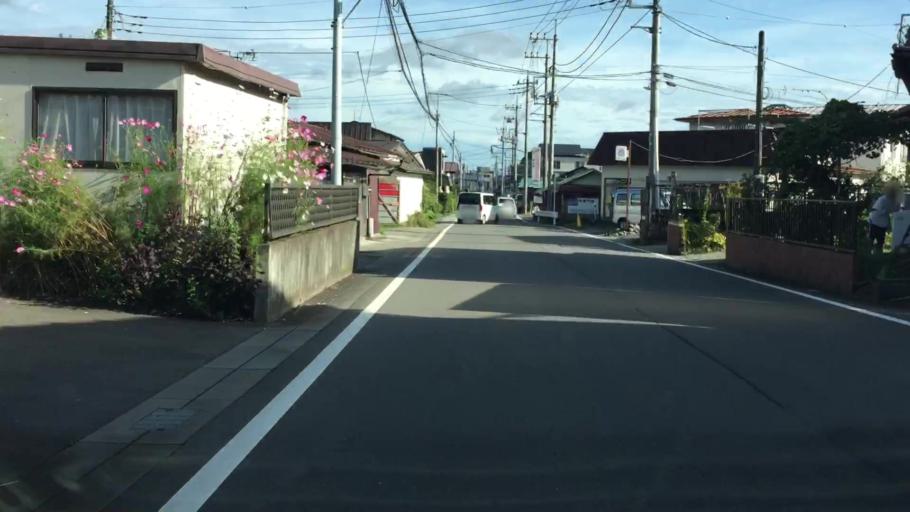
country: JP
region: Tochigi
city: Imaichi
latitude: 36.7362
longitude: 139.6860
